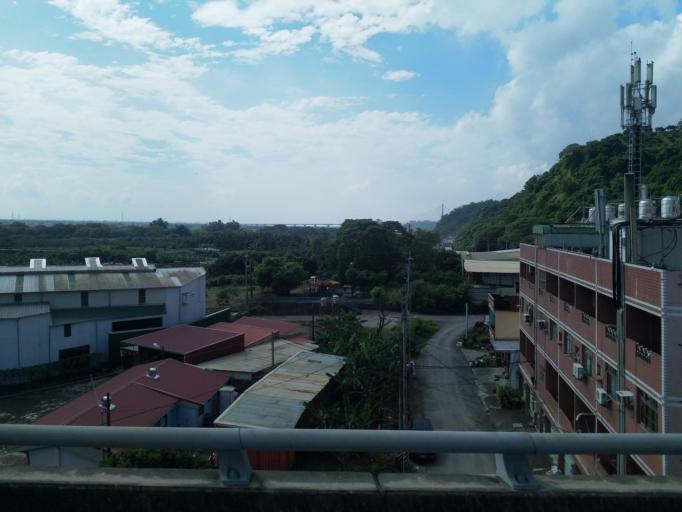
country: TW
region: Taiwan
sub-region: Pingtung
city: Pingtung
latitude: 22.7974
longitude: 120.4586
